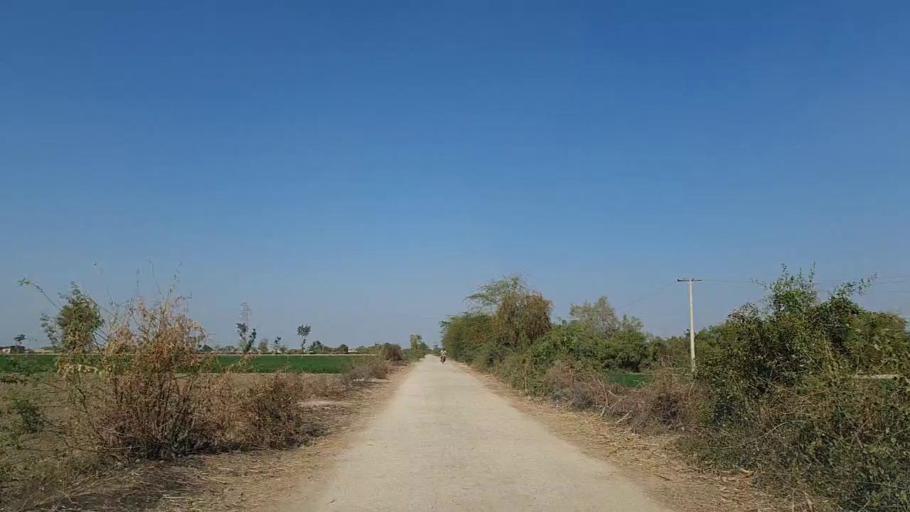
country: PK
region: Sindh
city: Nawabshah
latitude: 26.2493
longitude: 68.4410
